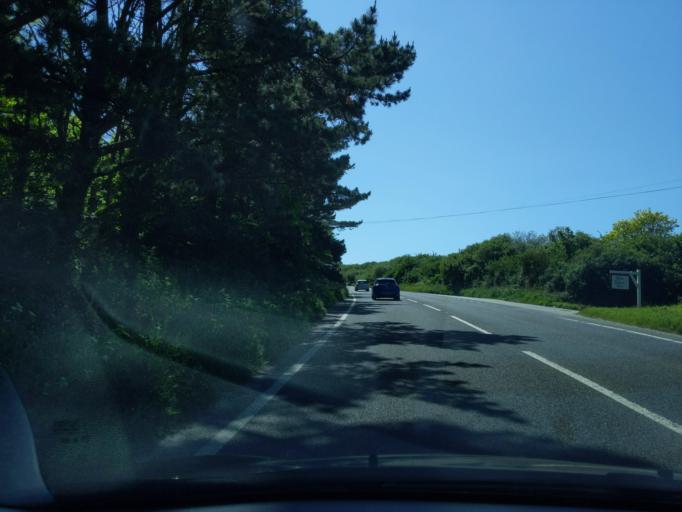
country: GB
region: England
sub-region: Cornwall
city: Penryn
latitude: 50.1708
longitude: -5.1429
